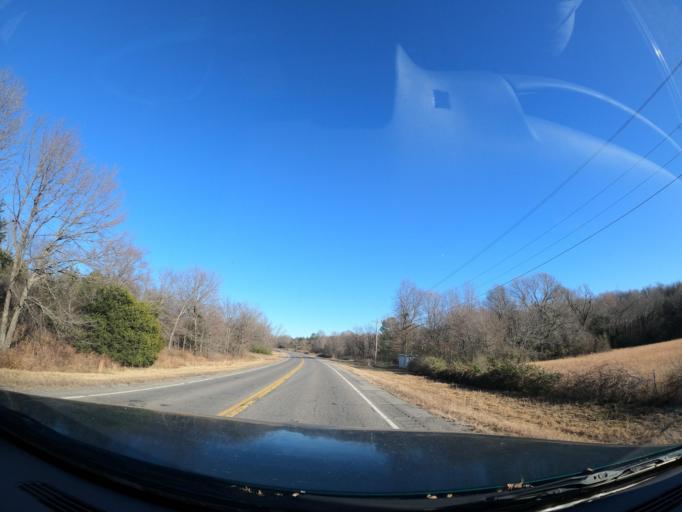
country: US
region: Oklahoma
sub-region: Pittsburg County
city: Longtown
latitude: 35.2141
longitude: -95.4162
